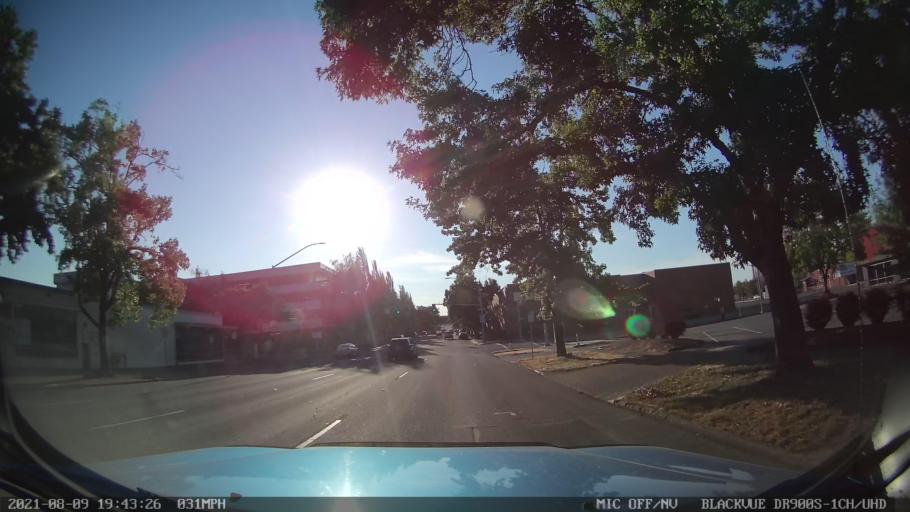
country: US
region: Oregon
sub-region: Marion County
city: Salem
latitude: 44.9433
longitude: -123.0325
